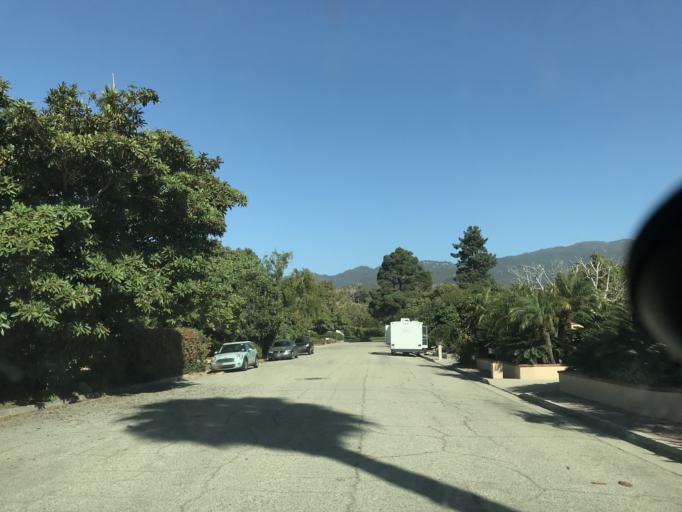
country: US
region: California
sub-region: Santa Barbara County
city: Goleta
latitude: 34.4524
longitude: -119.7980
